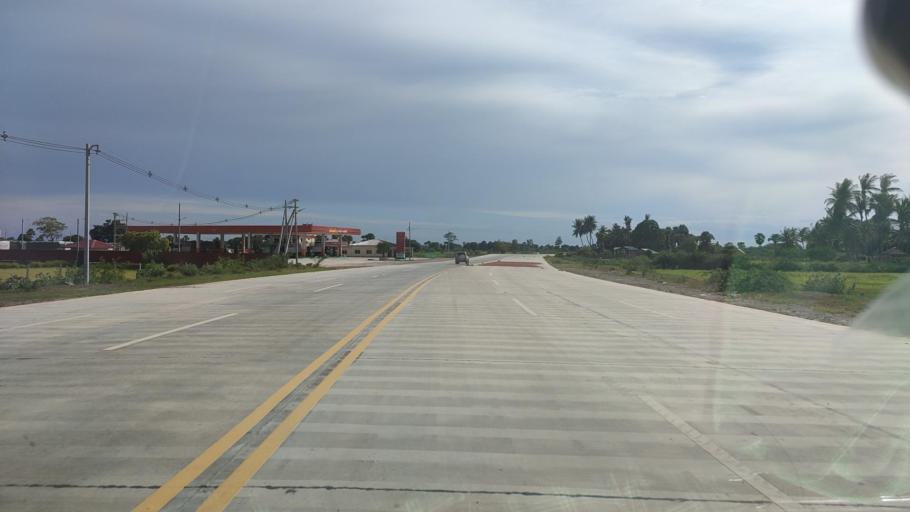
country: MM
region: Mandalay
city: Kyaukse
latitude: 21.6031
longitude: 96.1843
